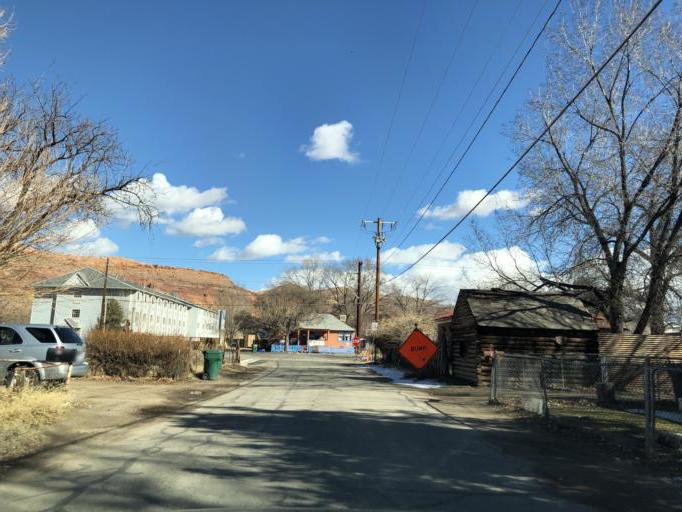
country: US
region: Utah
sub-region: Grand County
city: Moab
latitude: 38.5757
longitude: -109.5536
